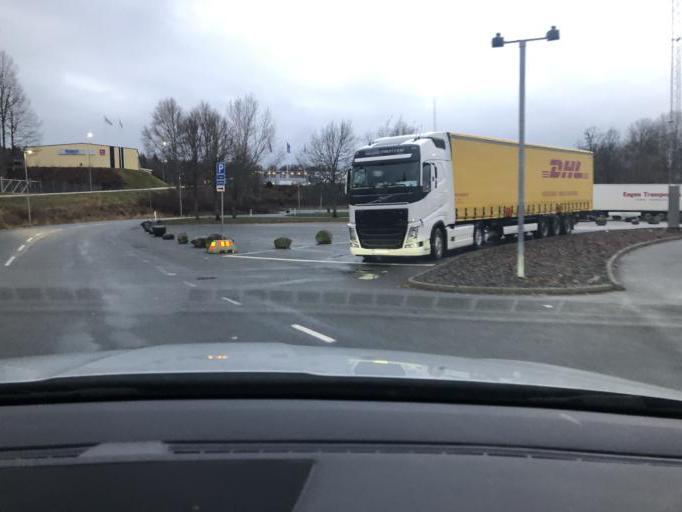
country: SE
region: Joenkoeping
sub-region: Jonkopings Kommun
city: Jonkoping
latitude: 57.7605
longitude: 14.1914
